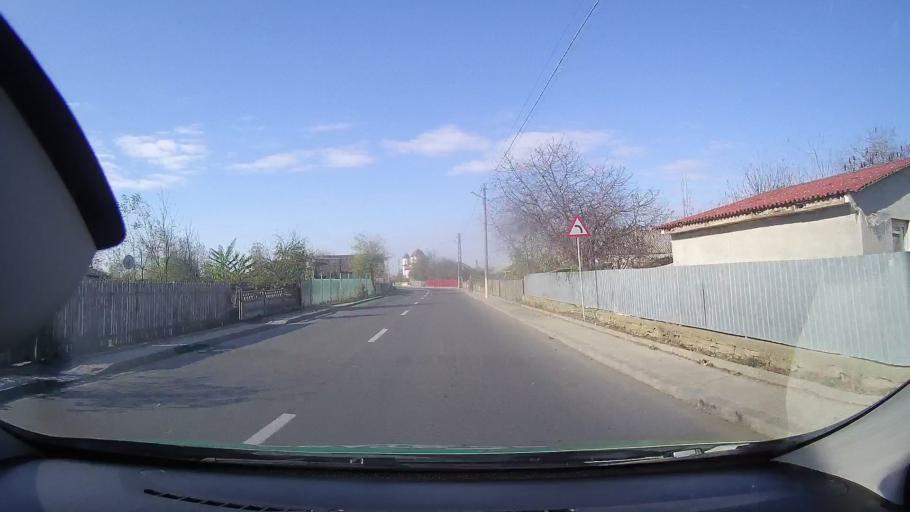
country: RO
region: Tulcea
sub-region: Comuna Murighiol
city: Murighiol
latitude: 45.0203
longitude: 29.1211
